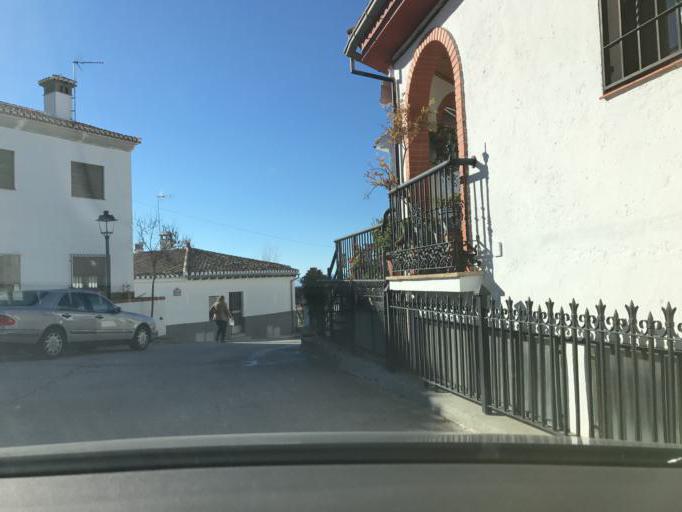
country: ES
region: Andalusia
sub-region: Provincia de Granada
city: Viznar
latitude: 37.2325
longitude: -3.5523
